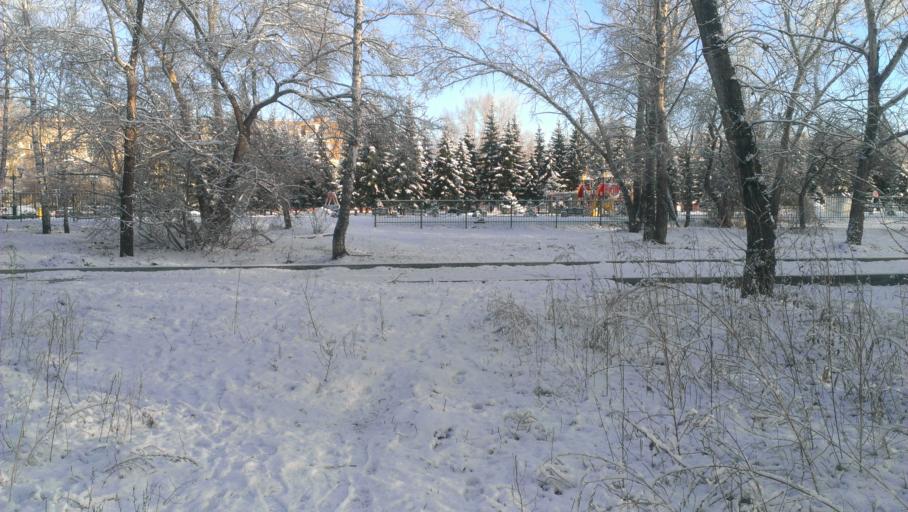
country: RU
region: Altai Krai
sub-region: Gorod Barnaulskiy
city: Barnaul
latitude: 53.3646
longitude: 83.6885
